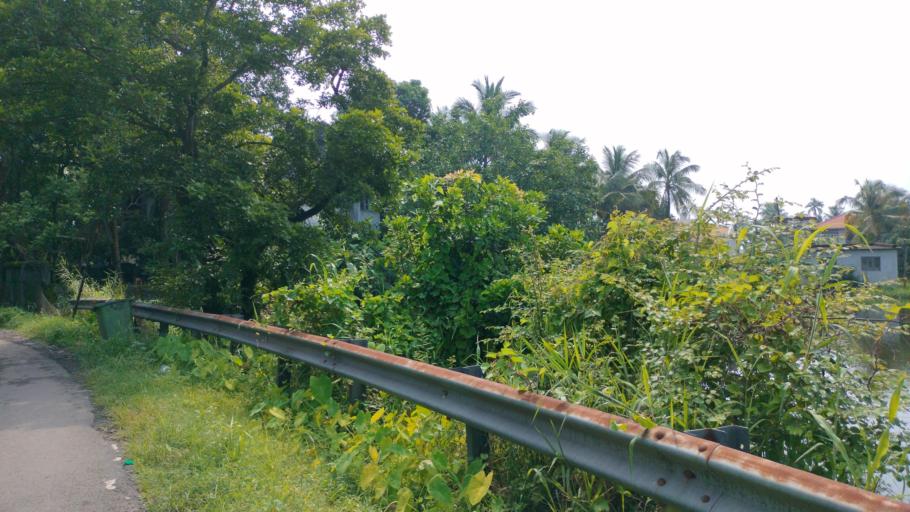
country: IN
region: Maharashtra
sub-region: Thane
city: Virar
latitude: 19.4146
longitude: 72.7922
